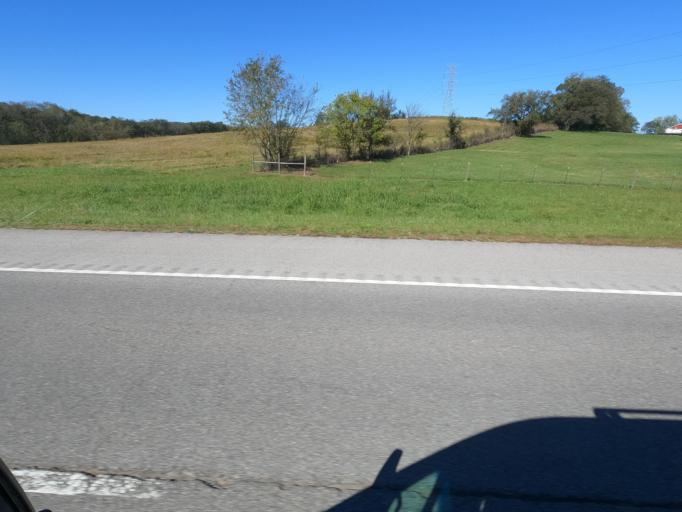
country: US
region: Tennessee
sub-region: Maury County
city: Mount Pleasant
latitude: 35.4908
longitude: -87.2380
